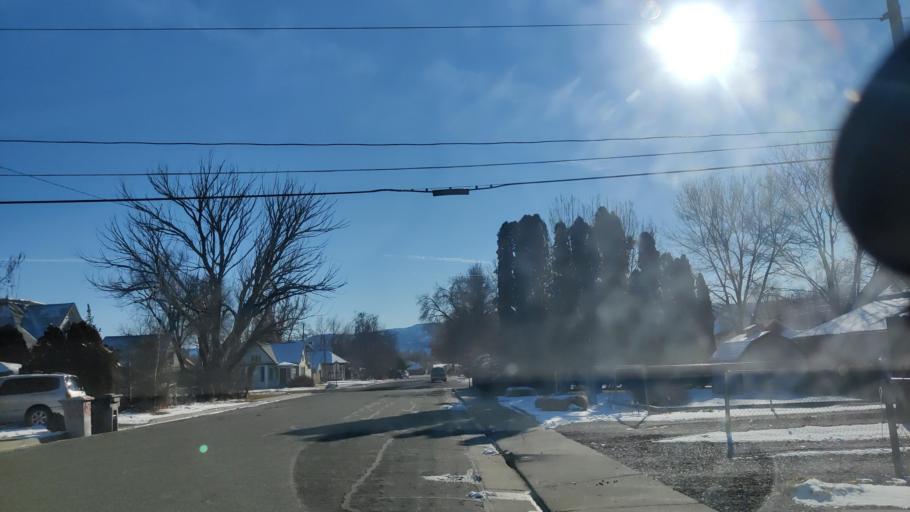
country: US
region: Colorado
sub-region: Mesa County
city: Fruita
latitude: 39.1595
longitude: -108.7279
